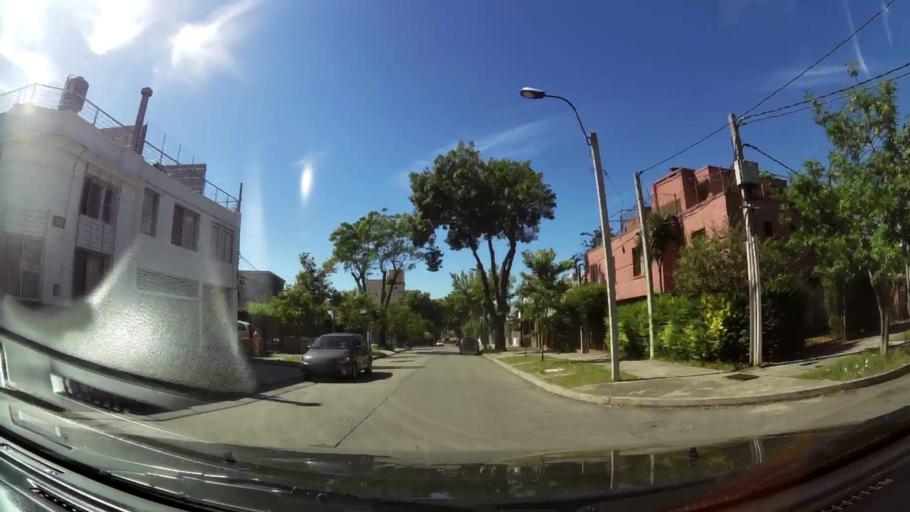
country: UY
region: Montevideo
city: Montevideo
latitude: -34.8908
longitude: -56.1226
